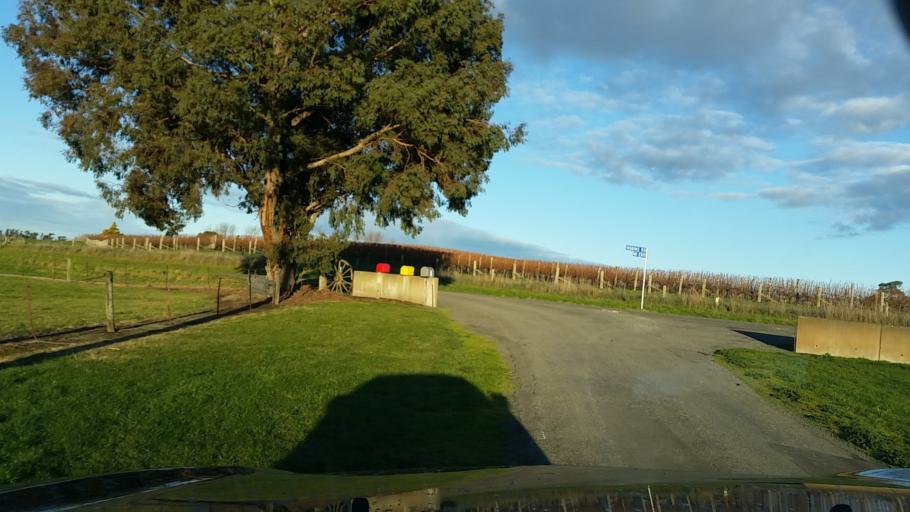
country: NZ
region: Marlborough
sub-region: Marlborough District
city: Blenheim
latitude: -41.6995
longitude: 173.9542
